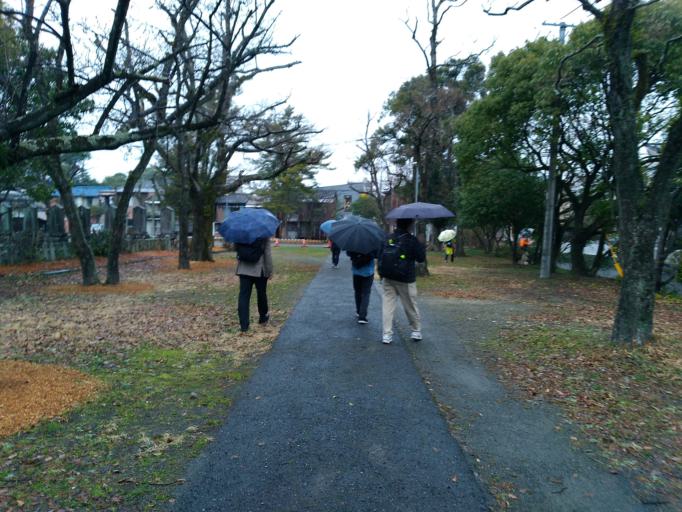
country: JP
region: Saga Prefecture
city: Saga-shi
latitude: 33.2485
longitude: 130.3036
